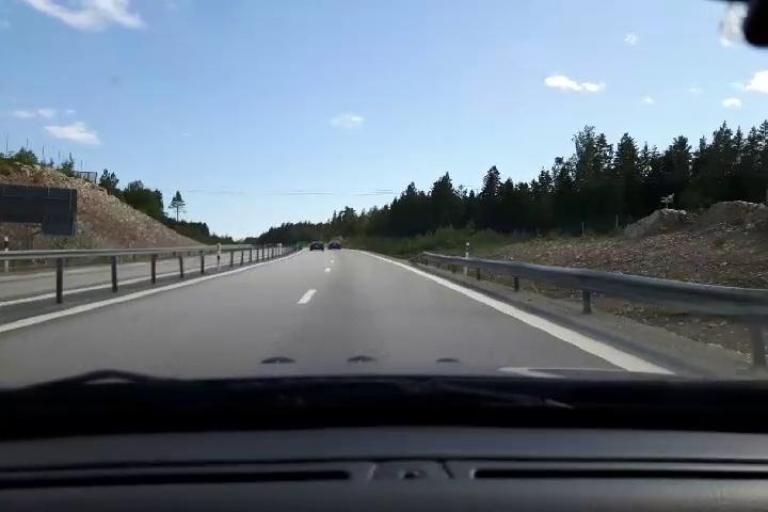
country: SE
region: Gaevleborg
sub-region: Hudiksvalls Kommun
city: Hudiksvall
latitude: 61.7105
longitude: 17.0485
